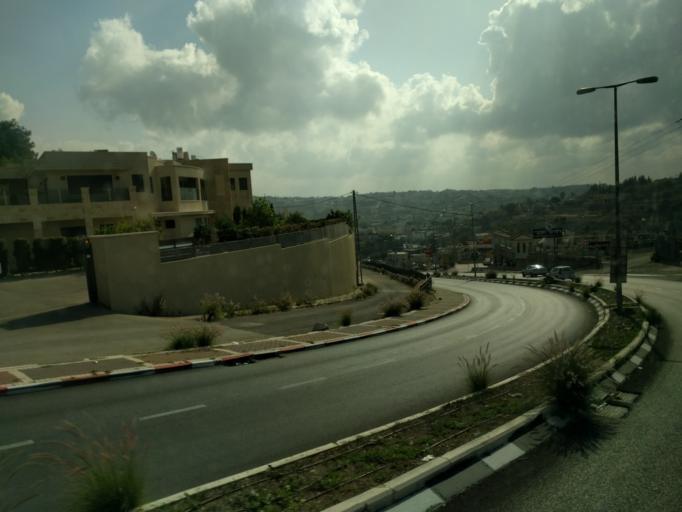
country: IL
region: Haifa
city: Daliyat el Karmil
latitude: 32.7056
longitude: 35.0576
